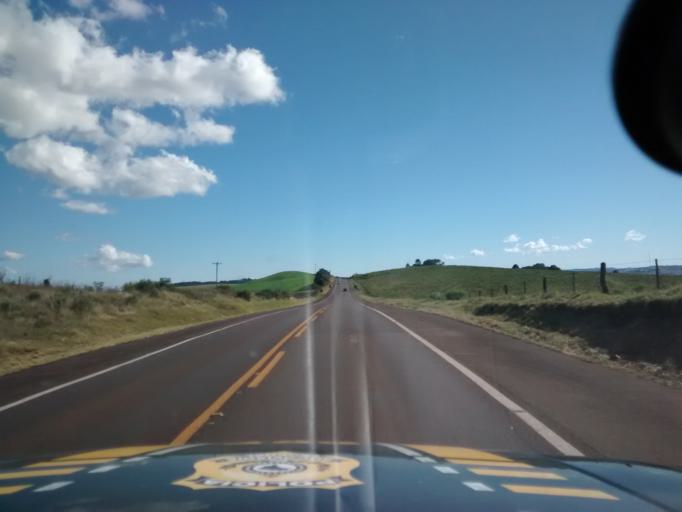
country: BR
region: Rio Grande do Sul
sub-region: Lagoa Vermelha
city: Lagoa Vermelha
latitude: -28.3246
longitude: -51.2553
